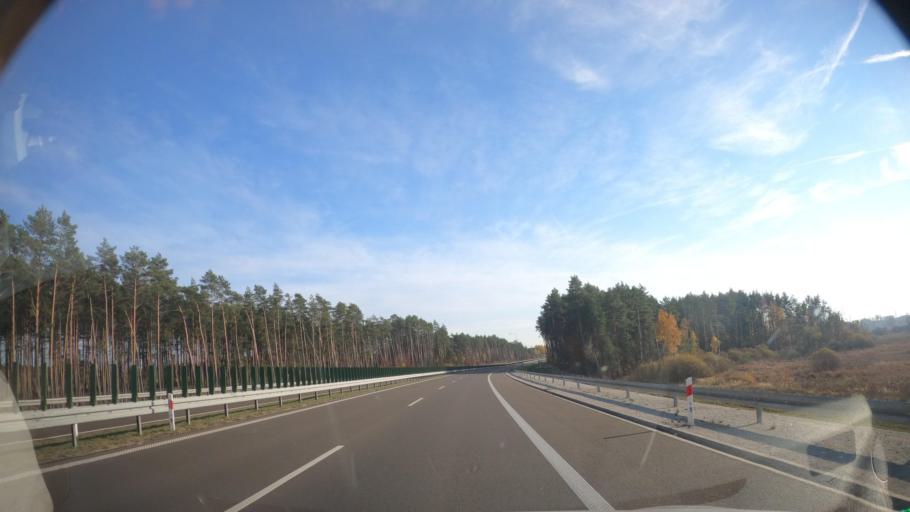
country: PL
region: West Pomeranian Voivodeship
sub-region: Powiat walecki
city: Walcz
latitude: 53.2918
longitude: 16.5005
